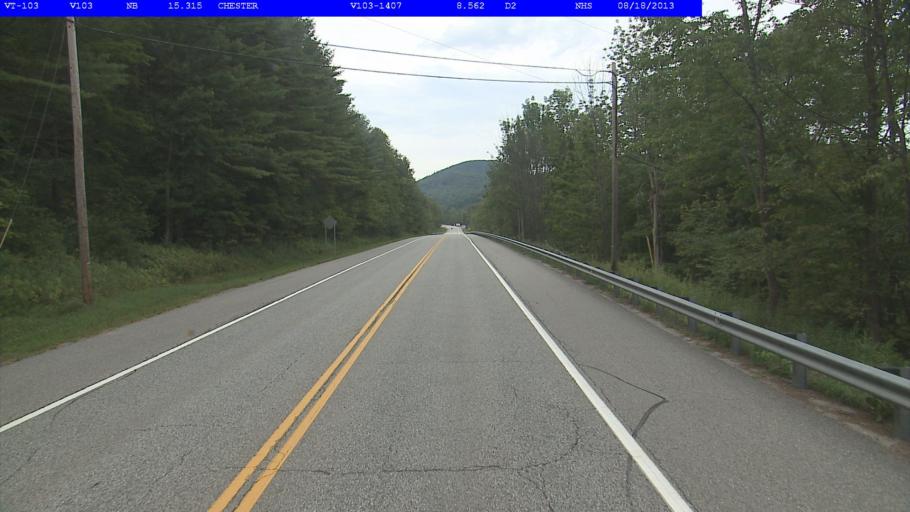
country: US
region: Vermont
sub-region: Windsor County
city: Chester
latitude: 43.3341
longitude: -72.6159
